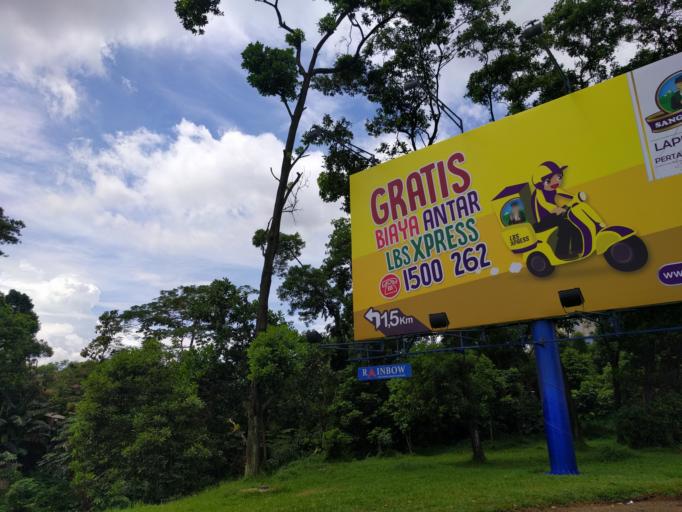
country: ID
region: West Java
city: Bogor
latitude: -6.6027
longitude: 106.8098
